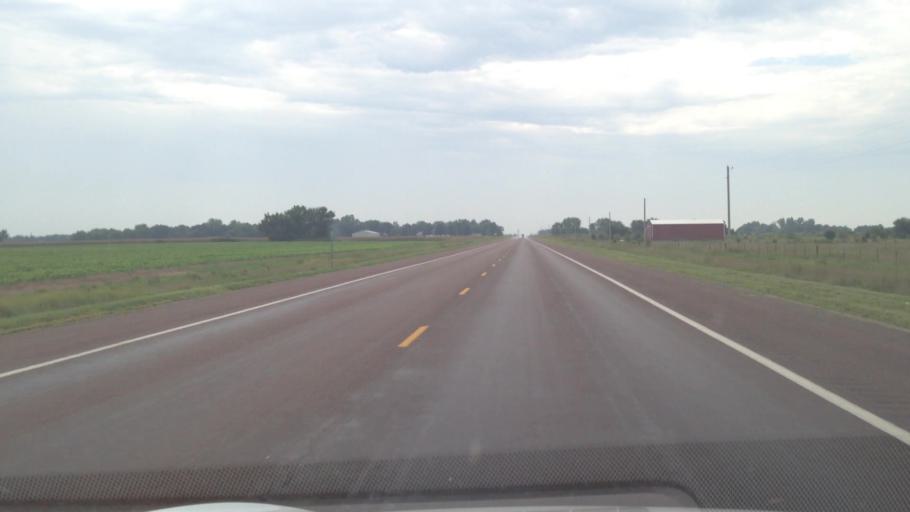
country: US
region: Kansas
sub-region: Crawford County
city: Girard
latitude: 37.4481
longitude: -94.8331
